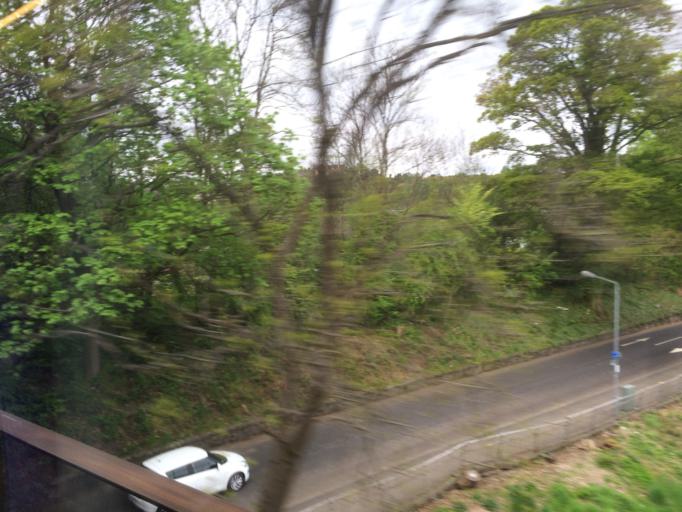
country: GB
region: Scotland
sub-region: Stirling
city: Stirling
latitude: 56.1266
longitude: -3.9352
